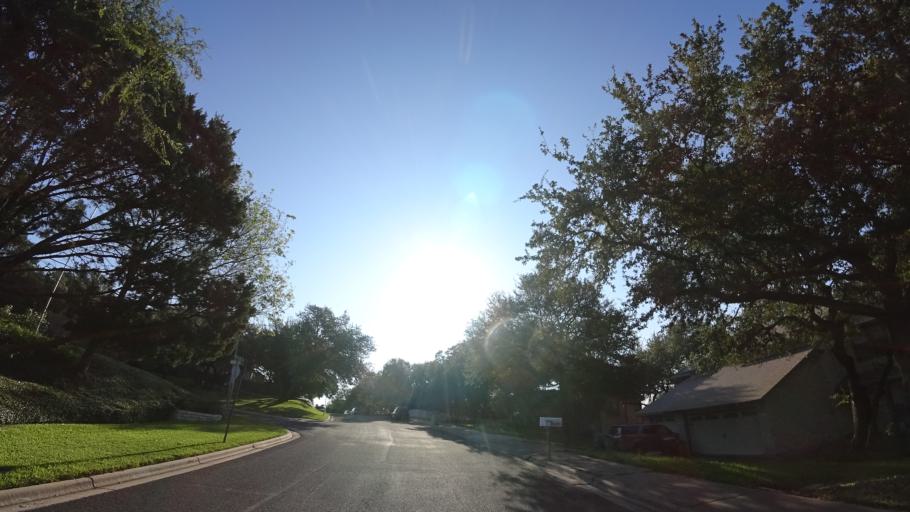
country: US
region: Texas
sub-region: Travis County
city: Rollingwood
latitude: 30.2607
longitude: -97.8016
